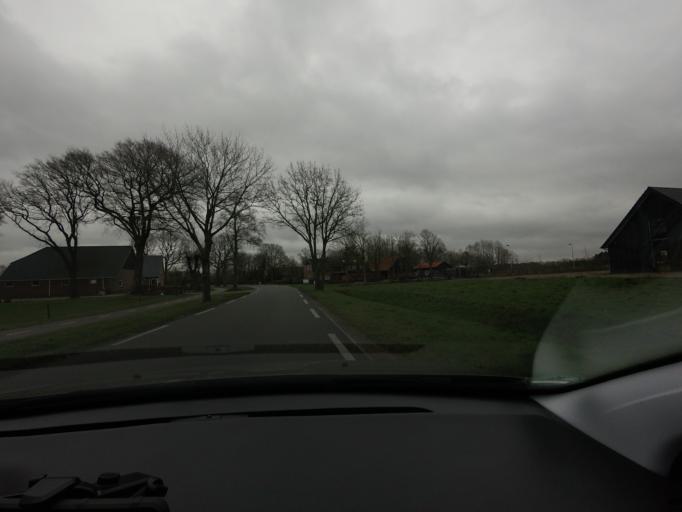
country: NL
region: Drenthe
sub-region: Gemeente Assen
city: Assen
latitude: 52.8516
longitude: 6.5510
